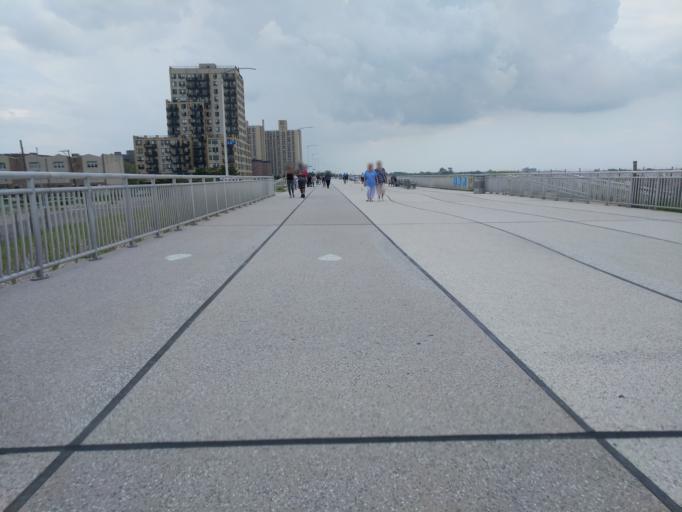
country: US
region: New York
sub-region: Nassau County
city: Atlantic Beach
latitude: 40.5921
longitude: -73.7611
